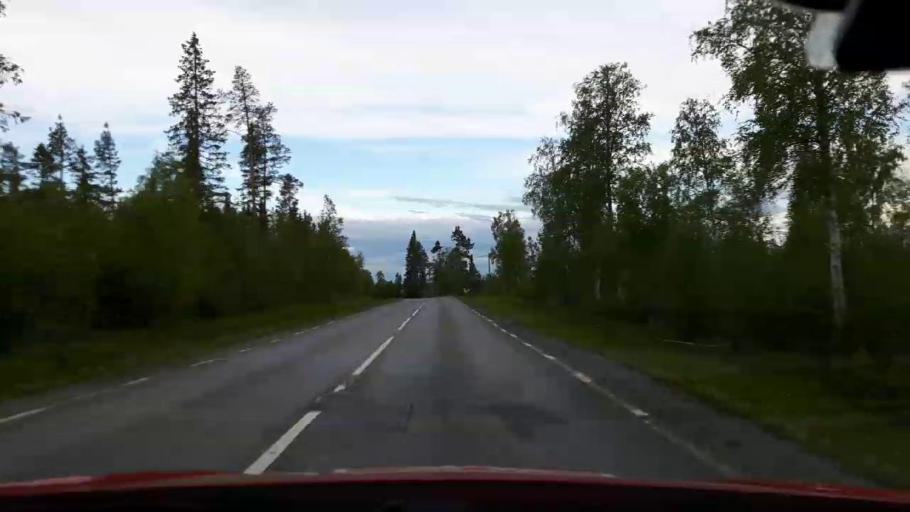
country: SE
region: Jaemtland
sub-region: Bergs Kommun
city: Hoverberg
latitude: 63.0000
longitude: 14.4838
